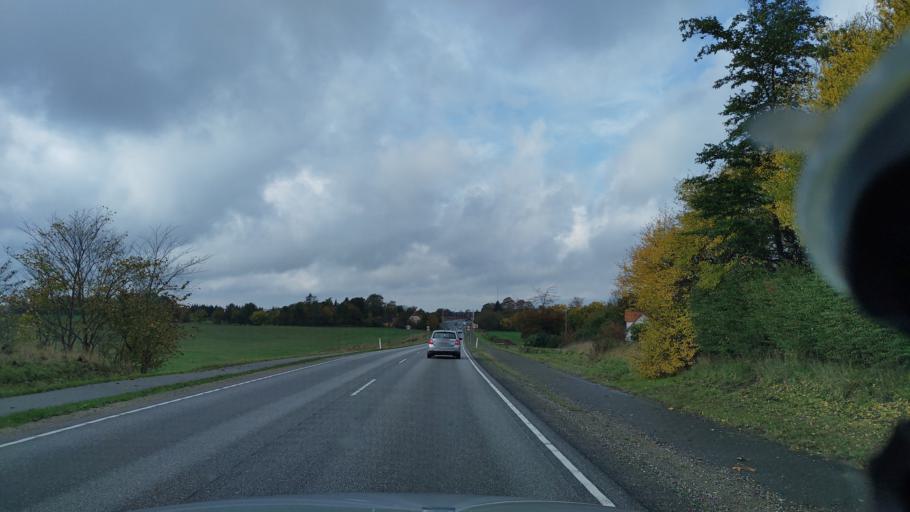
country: DK
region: Zealand
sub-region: Naestved Kommune
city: Fensmark
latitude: 55.2582
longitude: 11.8940
